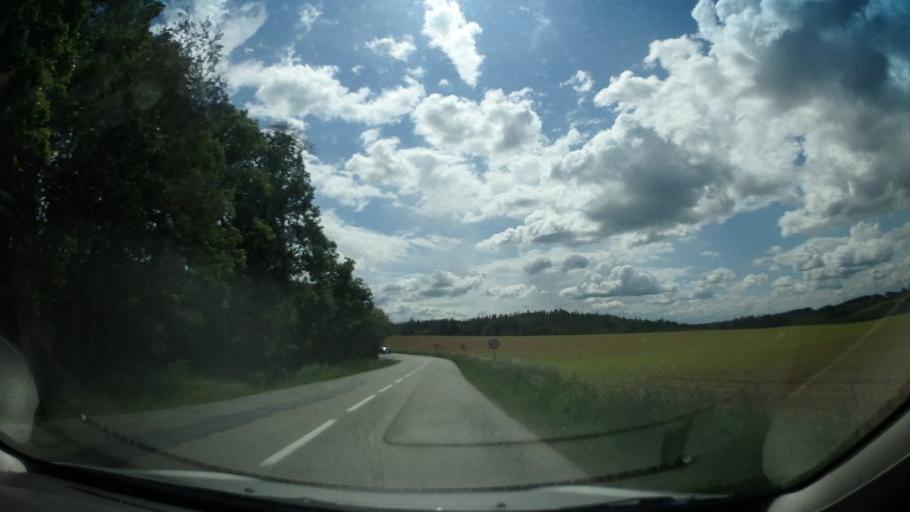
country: CZ
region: South Moravian
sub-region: Okres Blansko
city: Letovice
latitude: 49.5855
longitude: 16.5927
